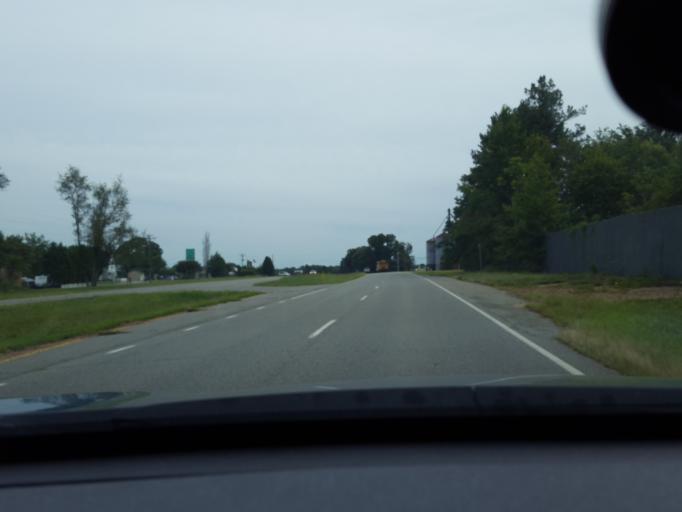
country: US
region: Virginia
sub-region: Caroline County
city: Bowling Green
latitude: 38.0211
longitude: -77.3391
